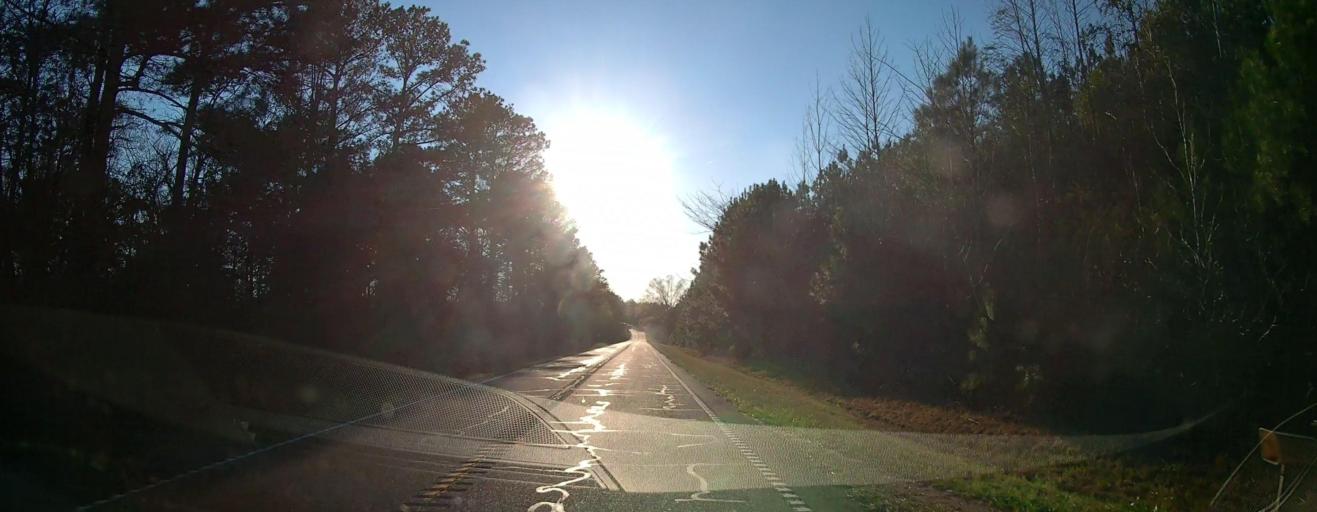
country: US
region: Georgia
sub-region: Talbot County
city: Talbotton
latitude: 32.6478
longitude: -84.6896
